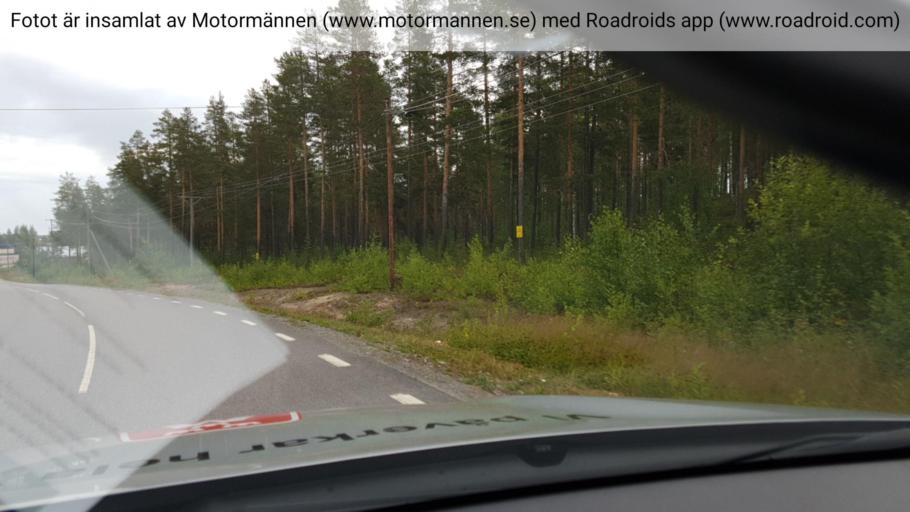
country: SE
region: Norrbotten
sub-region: Bodens Kommun
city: Boden
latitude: 65.7960
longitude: 21.6513
